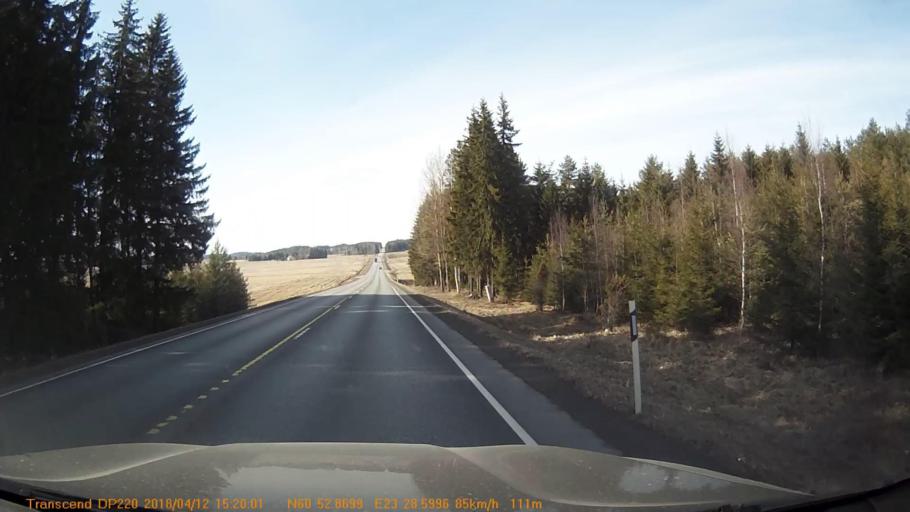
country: FI
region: Haeme
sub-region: Forssa
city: Jokioinen
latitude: 60.8814
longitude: 23.4762
